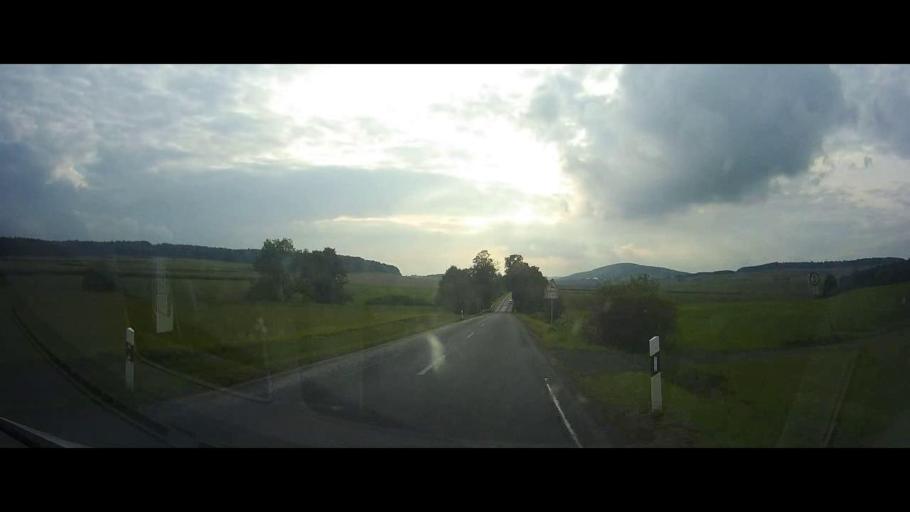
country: DE
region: Lower Saxony
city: Rosdorf
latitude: 51.5565
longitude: 9.8578
